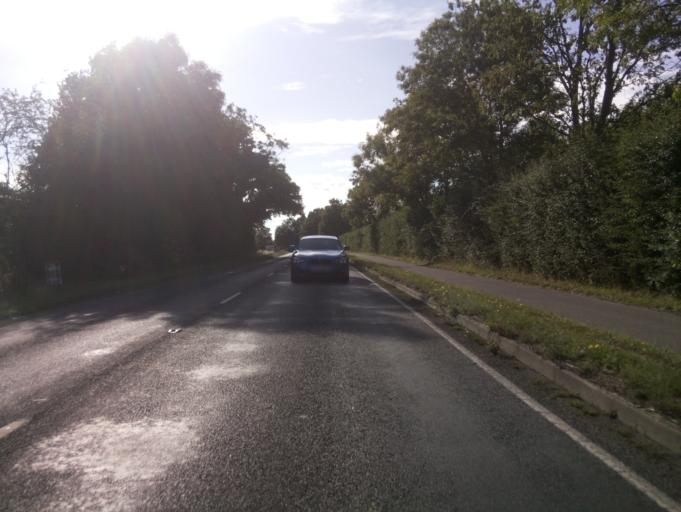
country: GB
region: England
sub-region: Hampshire
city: Romsey
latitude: 50.9844
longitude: -1.4584
